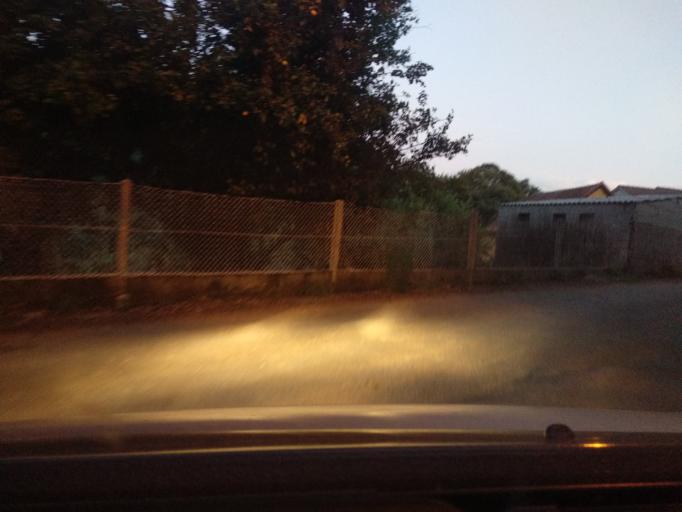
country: ES
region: Galicia
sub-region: Provincia de Pontevedra
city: Moana
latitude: 42.2877
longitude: -8.7511
